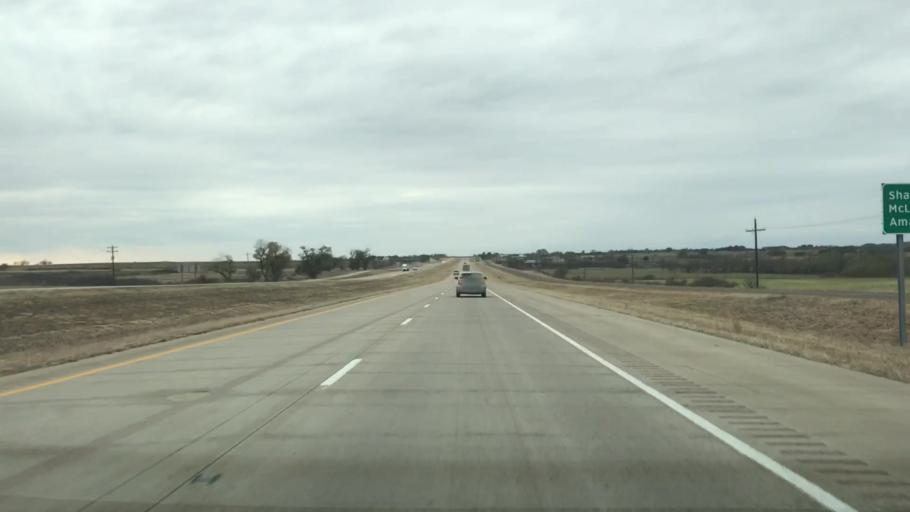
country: US
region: Texas
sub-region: Wheeler County
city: Shamrock
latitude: 35.2270
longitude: -100.1480
